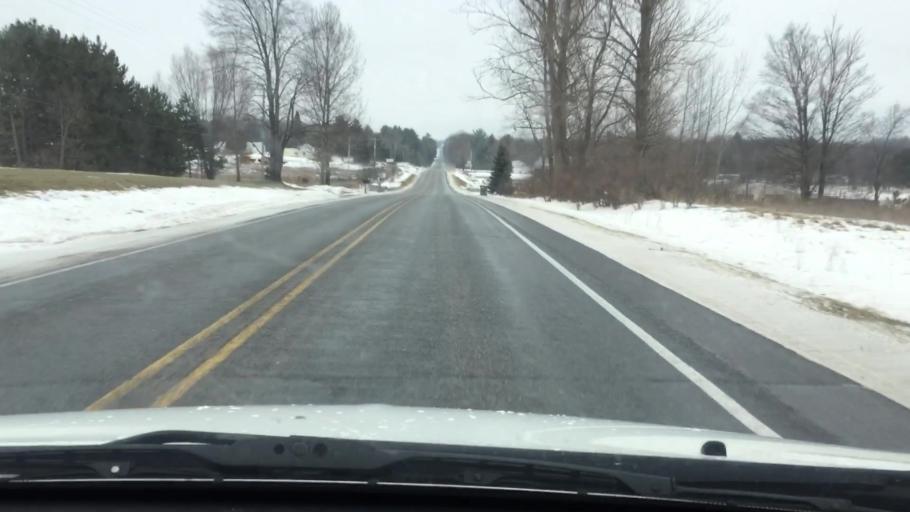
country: US
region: Michigan
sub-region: Wexford County
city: Cadillac
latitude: 44.0640
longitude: -85.4440
